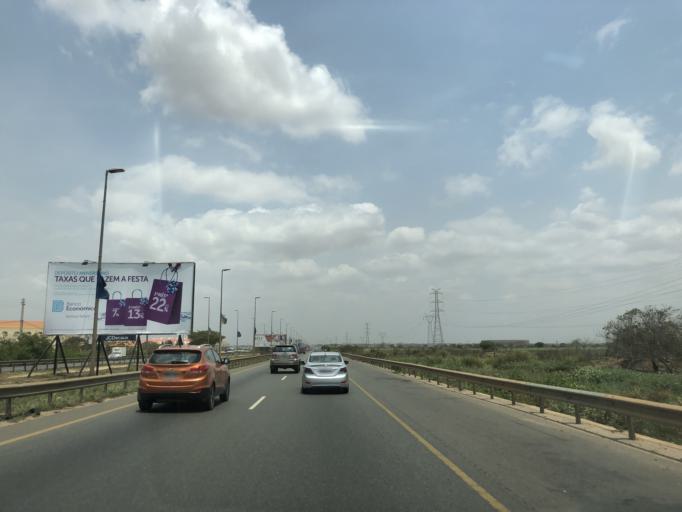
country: AO
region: Luanda
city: Luanda
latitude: -8.9732
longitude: 13.2683
